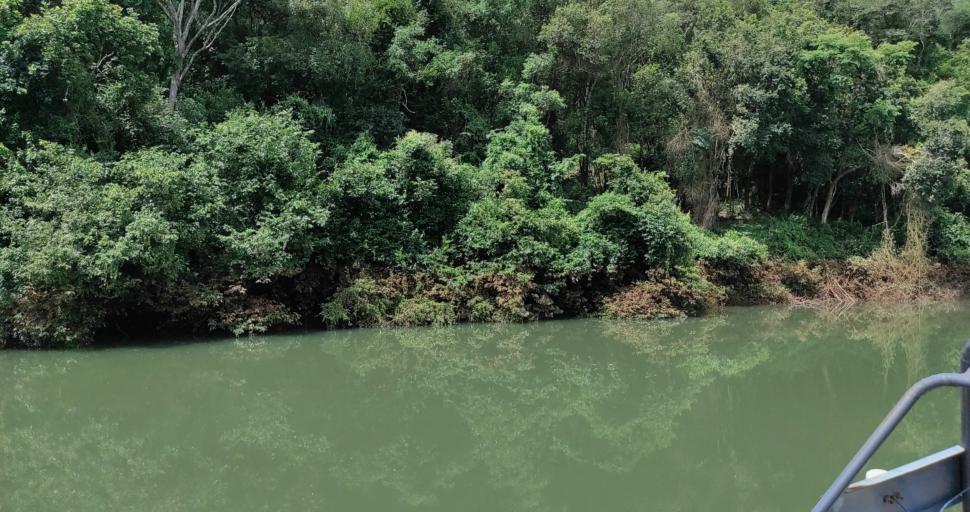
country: AR
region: Misiones
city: El Soberbio
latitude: -27.2820
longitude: -54.2019
